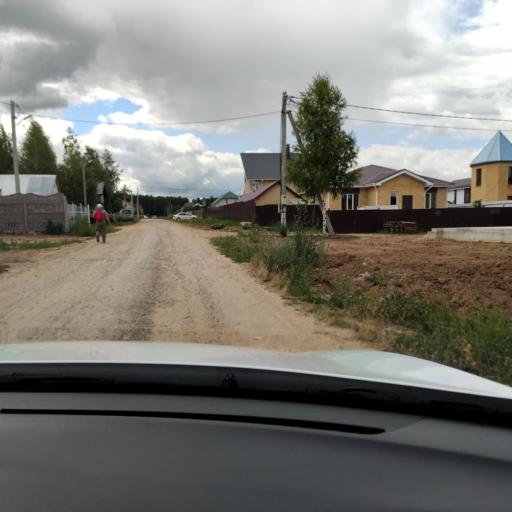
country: RU
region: Tatarstan
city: Vysokaya Gora
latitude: 55.7831
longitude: 49.2672
